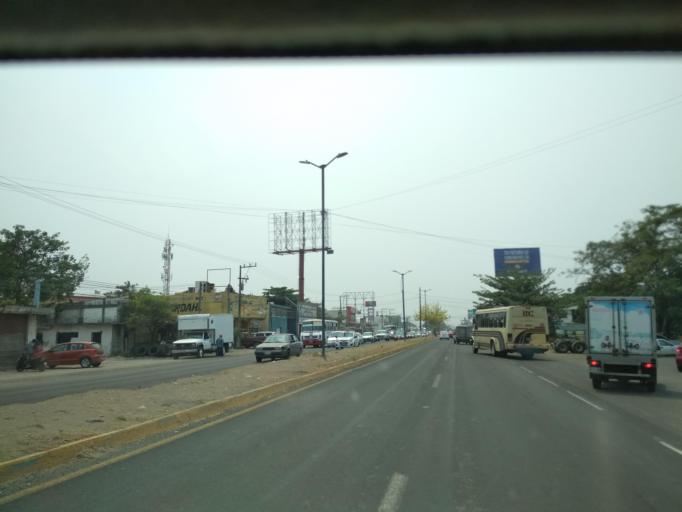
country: MX
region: Veracruz
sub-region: Veracruz
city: Las Amapolas
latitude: 19.1668
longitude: -96.2186
